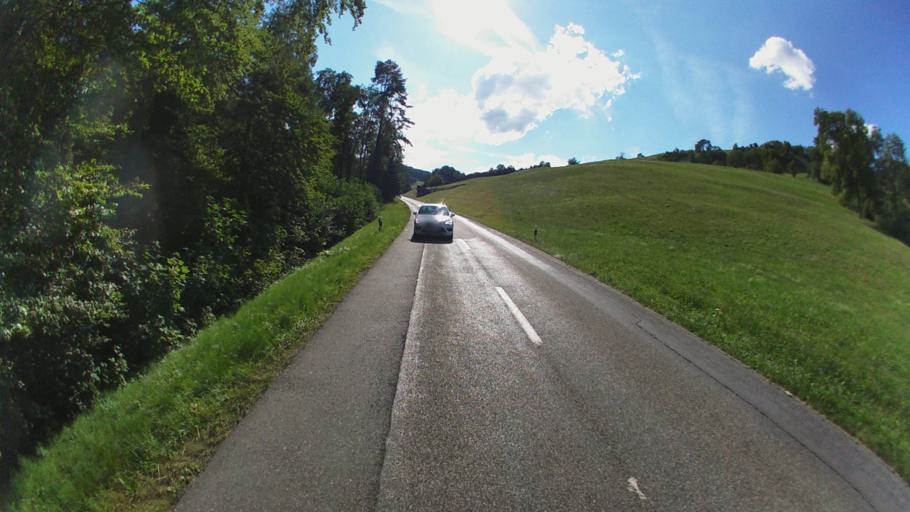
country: CH
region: Aargau
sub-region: Bezirk Rheinfelden
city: Wegenstetten
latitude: 47.4896
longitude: 7.9126
